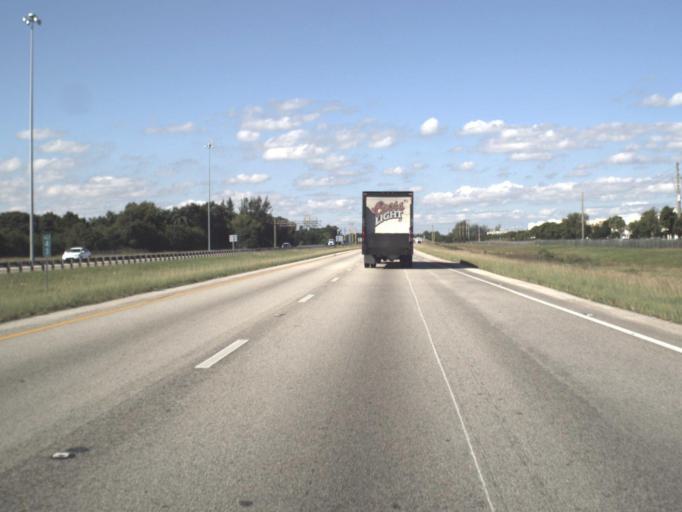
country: US
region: Florida
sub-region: Miami-Dade County
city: Country Club
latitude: 25.9710
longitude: -80.2978
